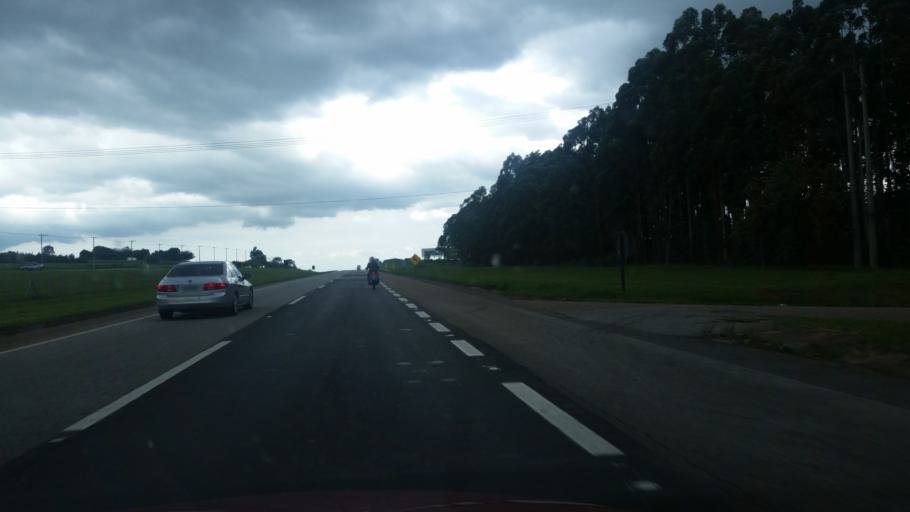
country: BR
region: Sao Paulo
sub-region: Porto Feliz
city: Porto Feliz
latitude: -23.3364
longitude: -47.5463
